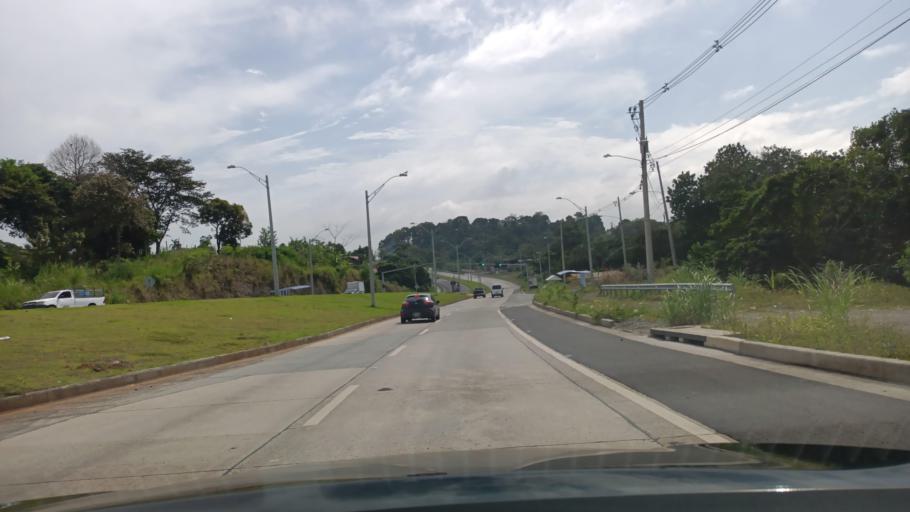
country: PA
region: Panama
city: Las Cumbres
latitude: 9.1007
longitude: -79.5166
